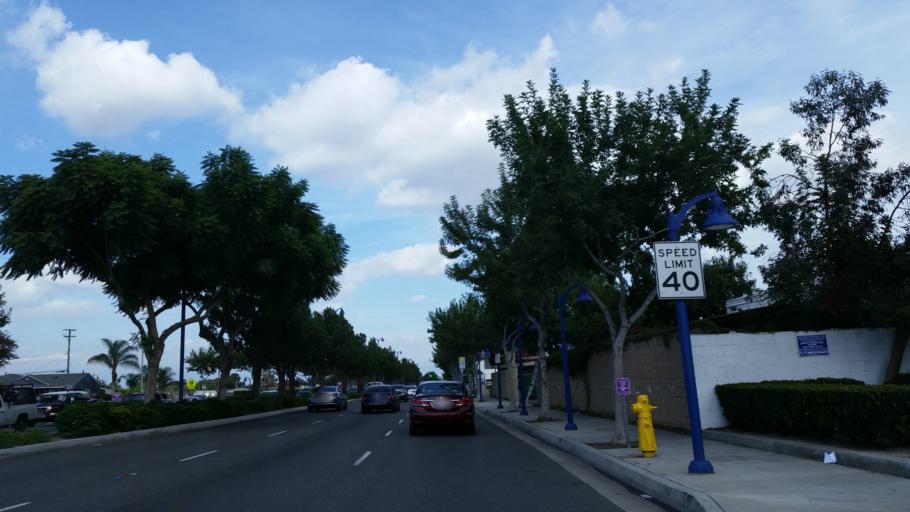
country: US
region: California
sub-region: Los Angeles County
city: Downey
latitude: 33.9174
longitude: -118.1373
